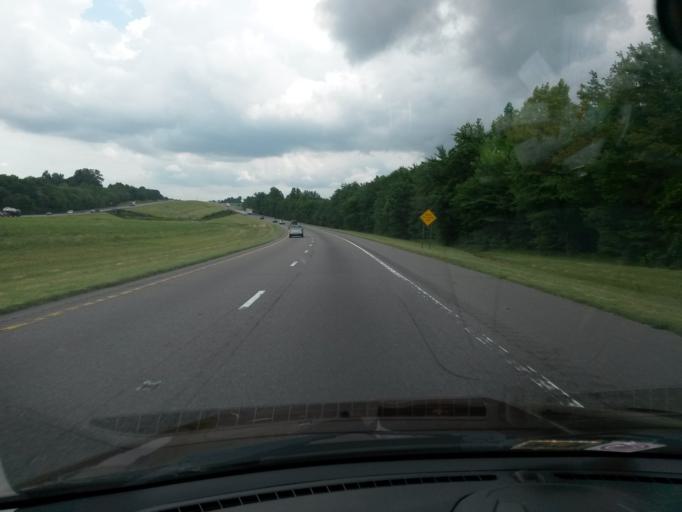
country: US
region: North Carolina
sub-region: Iredell County
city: Statesville
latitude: 35.9320
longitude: -80.8562
